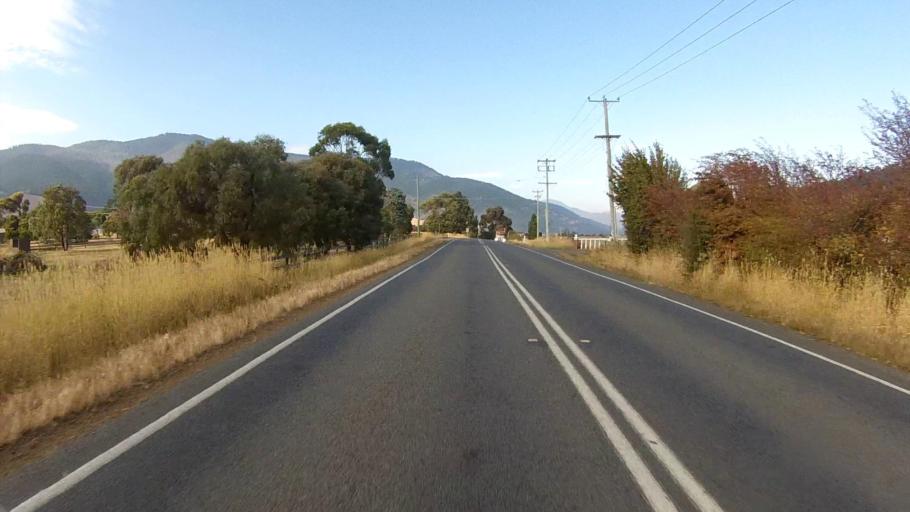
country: AU
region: Tasmania
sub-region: Brighton
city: Bridgewater
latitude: -42.7332
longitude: 147.1764
